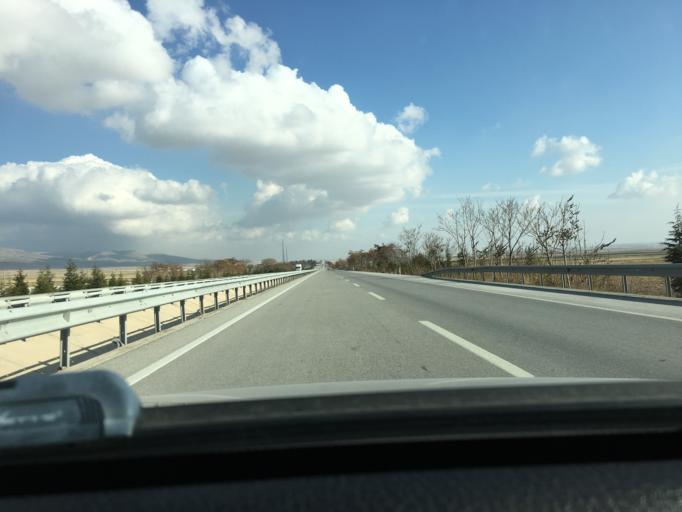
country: TR
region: Eskisehir
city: Kaymaz
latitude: 39.4806
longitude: 31.3029
